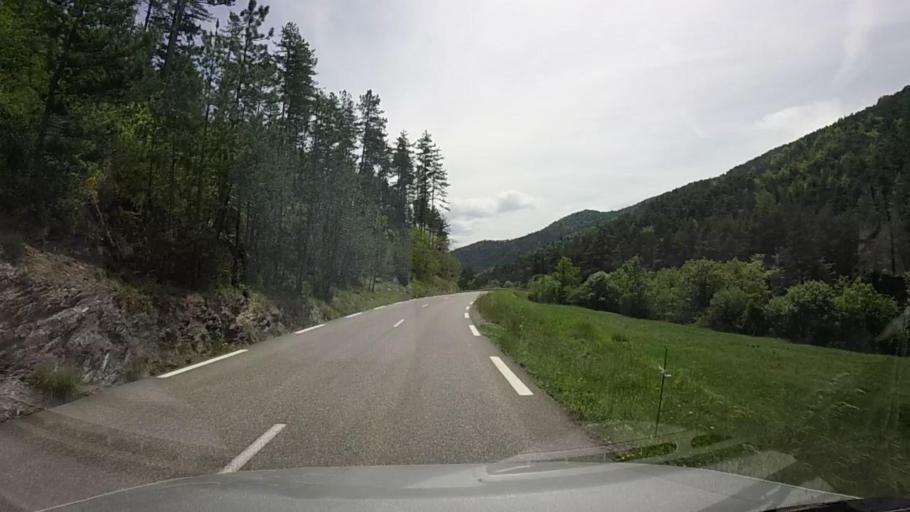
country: FR
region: Provence-Alpes-Cote d'Azur
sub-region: Departement des Alpes-de-Haute-Provence
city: Le Brusquet
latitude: 44.2192
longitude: 6.3608
